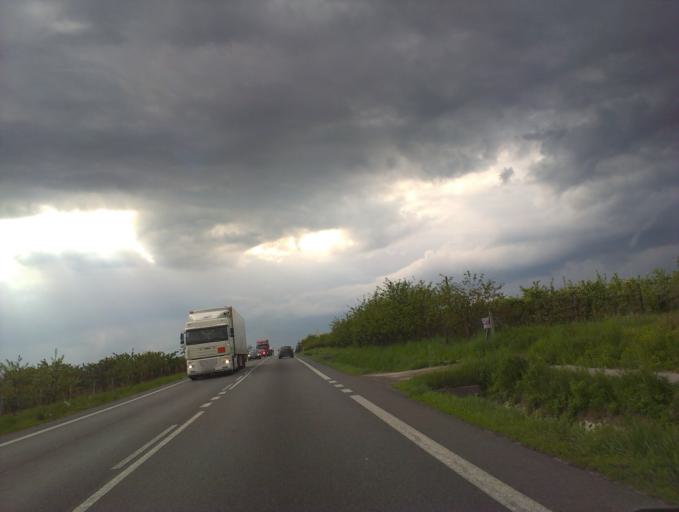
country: PL
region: Masovian Voivodeship
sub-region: Powiat grojecki
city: Pniewy
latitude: 51.9008
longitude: 20.7681
